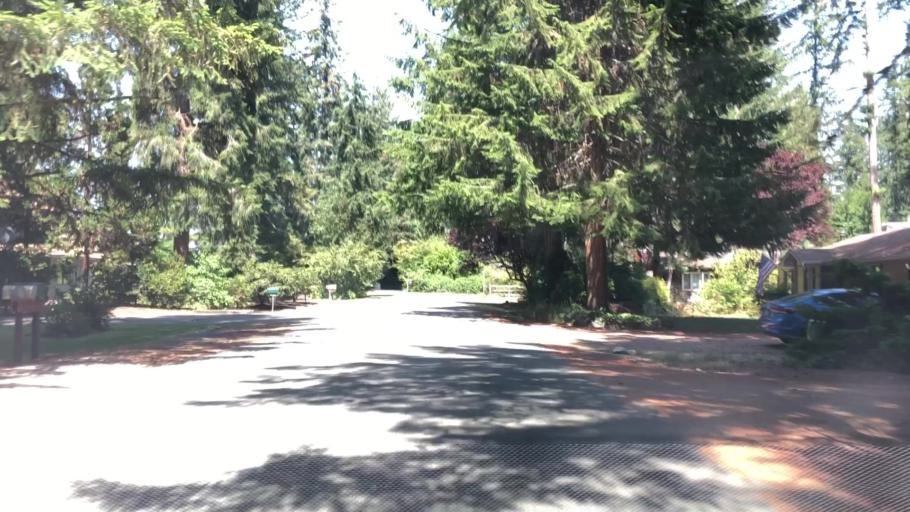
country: US
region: Washington
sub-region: King County
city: Cottage Lake
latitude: 47.7485
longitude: -122.0879
